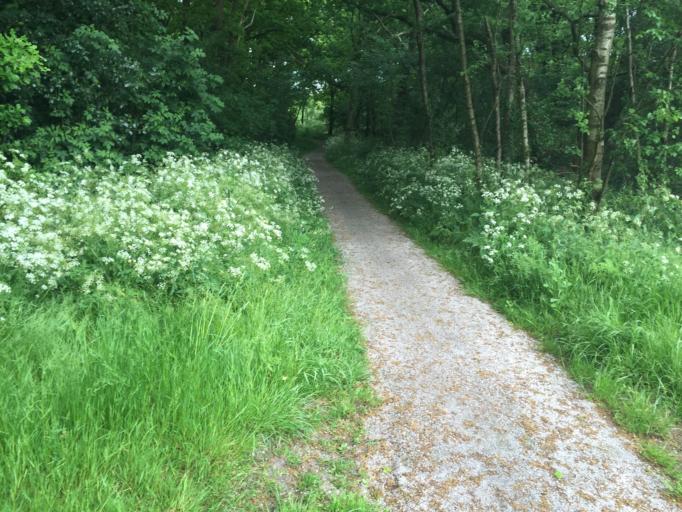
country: NL
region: Drenthe
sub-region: Gemeente Westerveld
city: Havelte
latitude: 52.7859
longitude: 6.2147
